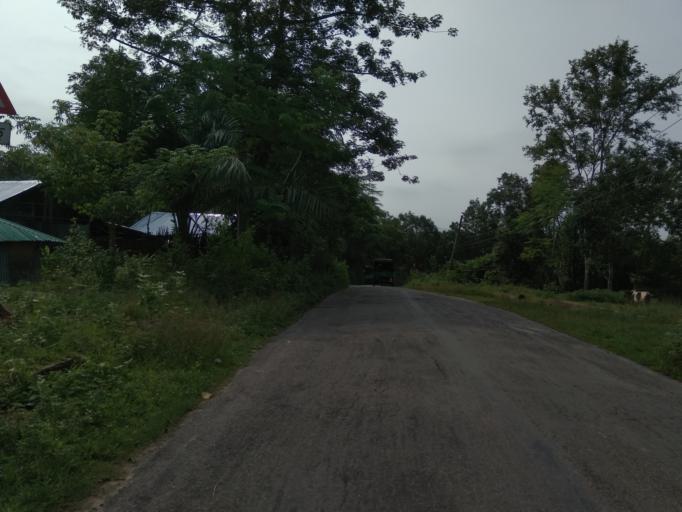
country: BD
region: Chittagong
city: Khagrachhari
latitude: 22.9964
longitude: 92.0118
